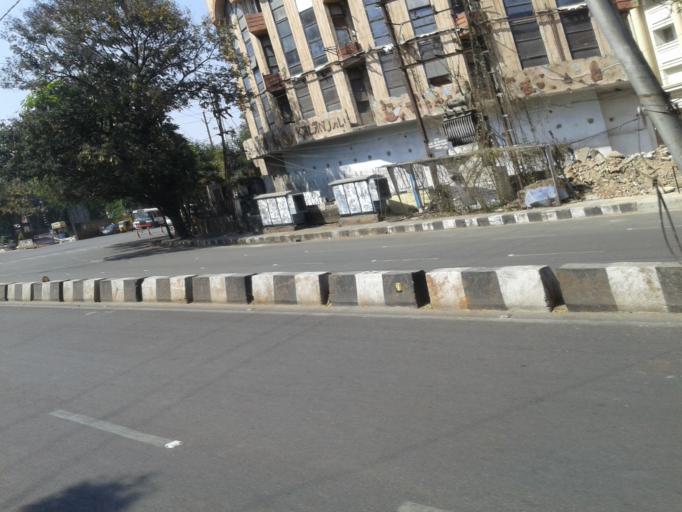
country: IN
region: Telangana
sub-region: Hyderabad
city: Hyderabad
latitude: 17.4009
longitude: 78.4711
